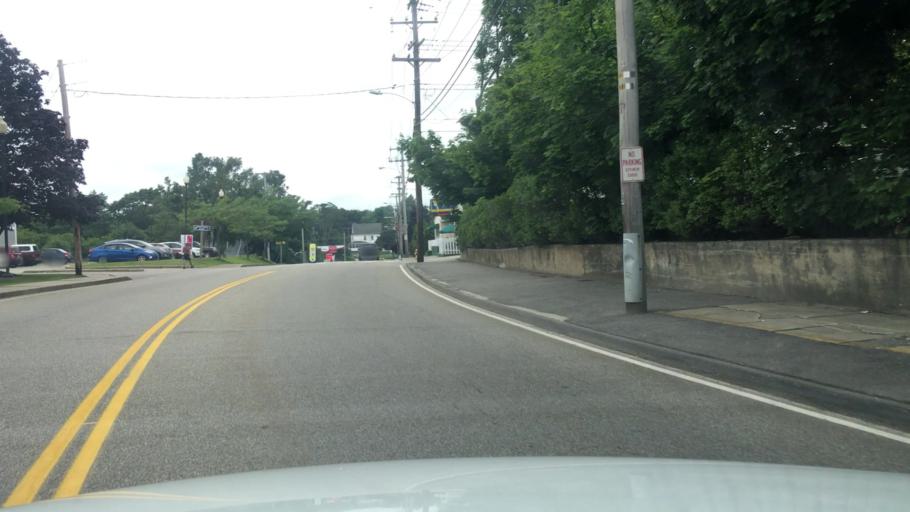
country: US
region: Maine
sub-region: York County
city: Old Orchard Beach
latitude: 43.5166
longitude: -70.3780
